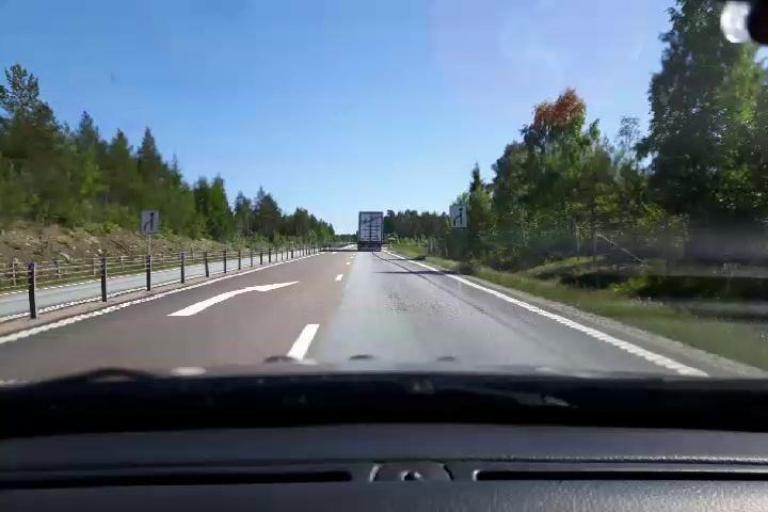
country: SE
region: Gaevleborg
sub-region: Soderhamns Kommun
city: Soderhamn
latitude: 61.2657
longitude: 17.0299
